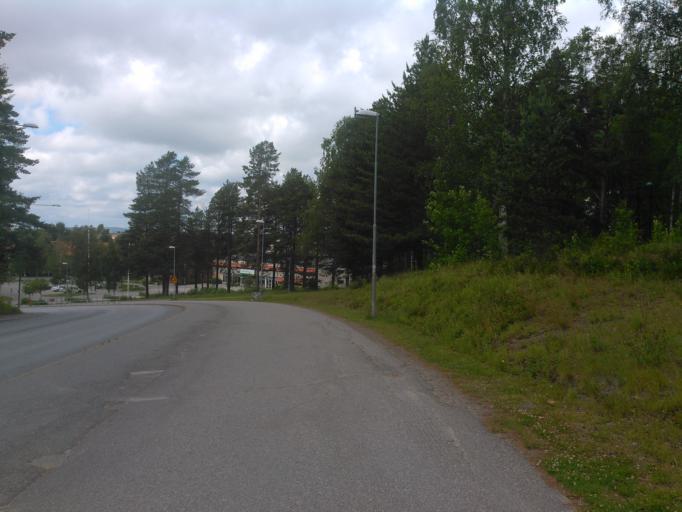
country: SE
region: Vaesterbotten
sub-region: Umea Kommun
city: Umea
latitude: 63.8279
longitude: 20.2897
